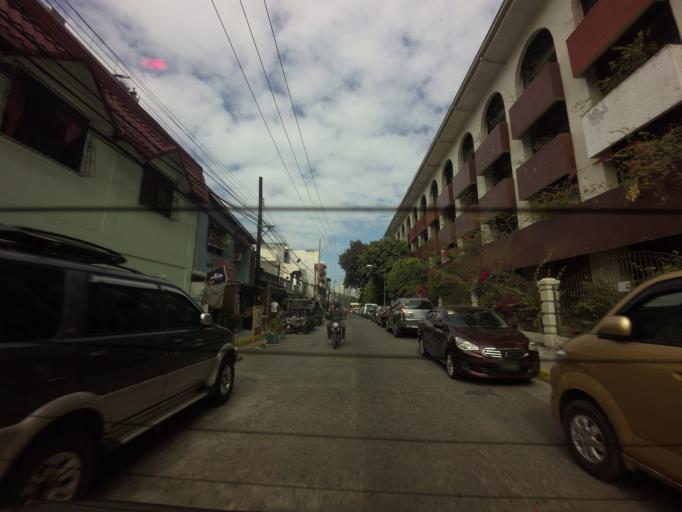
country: PH
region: Metro Manila
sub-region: Makati City
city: Makati City
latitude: 14.5593
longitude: 121.0428
